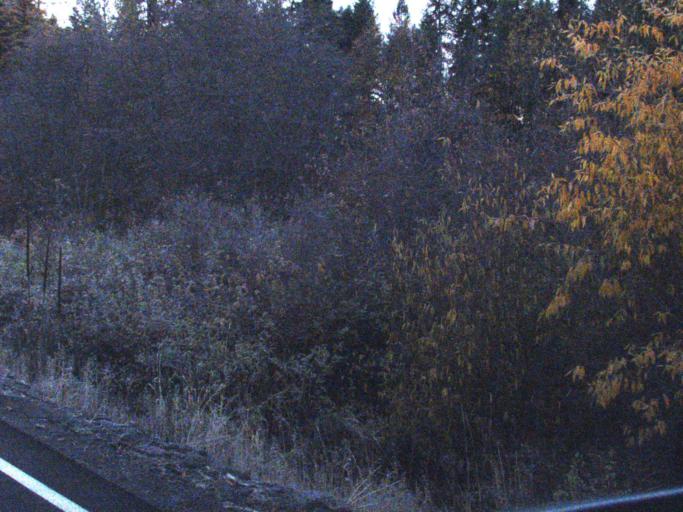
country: US
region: Washington
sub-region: Ferry County
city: Republic
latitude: 48.4315
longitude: -118.7309
